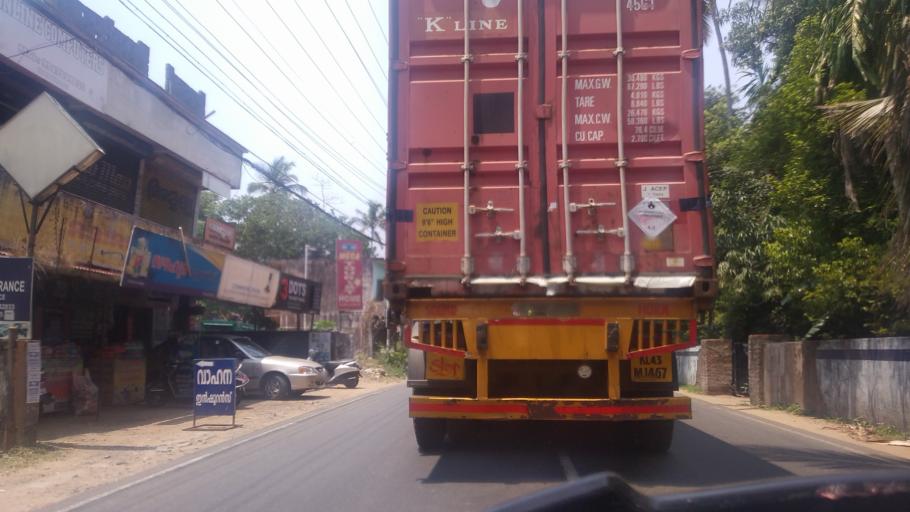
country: IN
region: Kerala
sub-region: Thrissur District
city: Kodungallur
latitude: 10.2404
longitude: 76.1922
